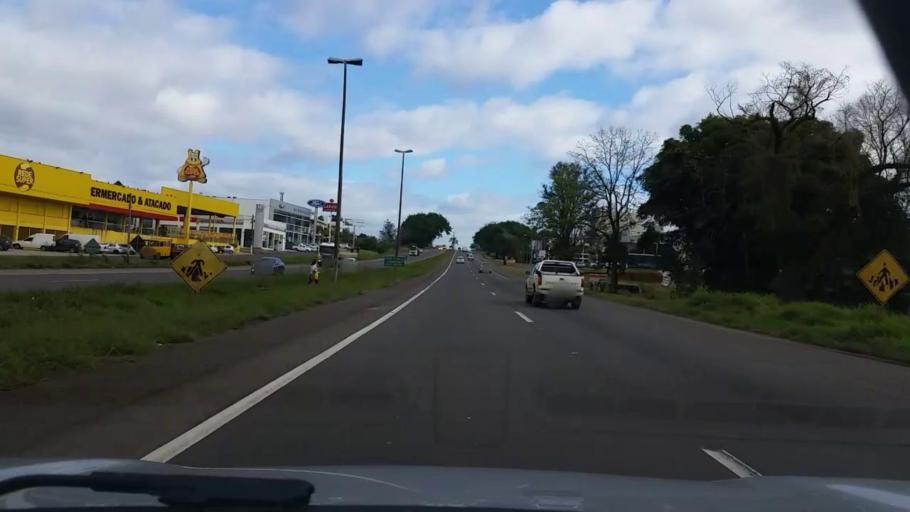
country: BR
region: Rio Grande do Sul
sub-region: Lajeado
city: Lajeado
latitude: -29.4541
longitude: -51.9608
